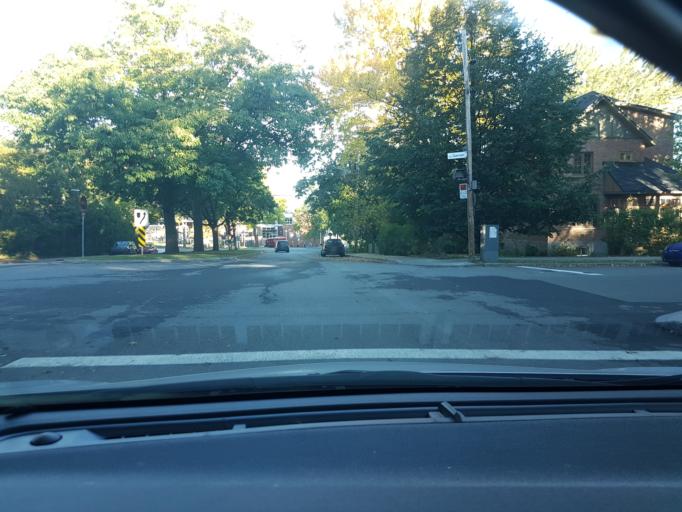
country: CA
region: Quebec
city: Quebec
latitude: 46.7929
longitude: -71.2605
